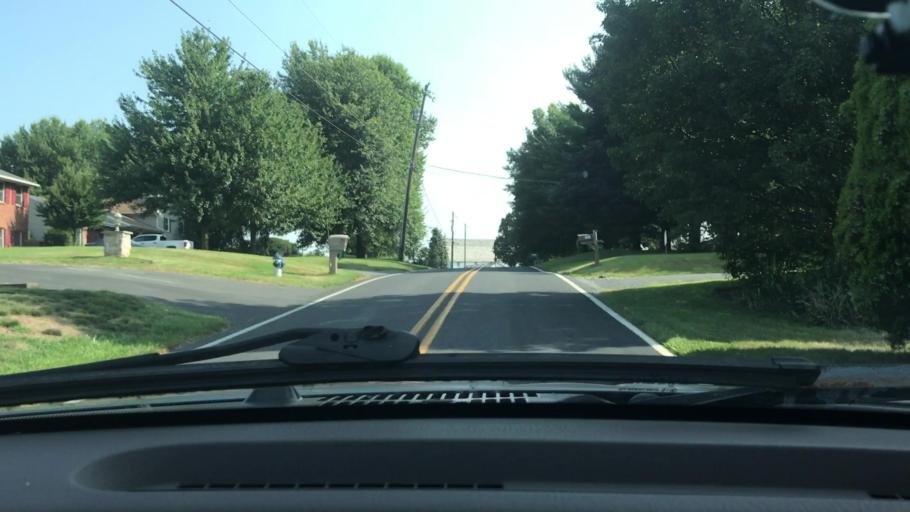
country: US
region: Pennsylvania
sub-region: Lancaster County
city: Rheems
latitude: 40.1464
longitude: -76.5717
